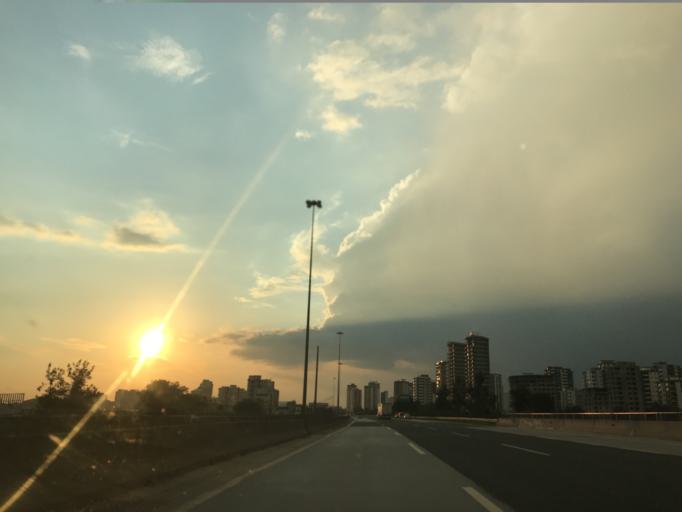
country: TR
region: Adana
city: Seyhan
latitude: 37.0327
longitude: 35.2543
